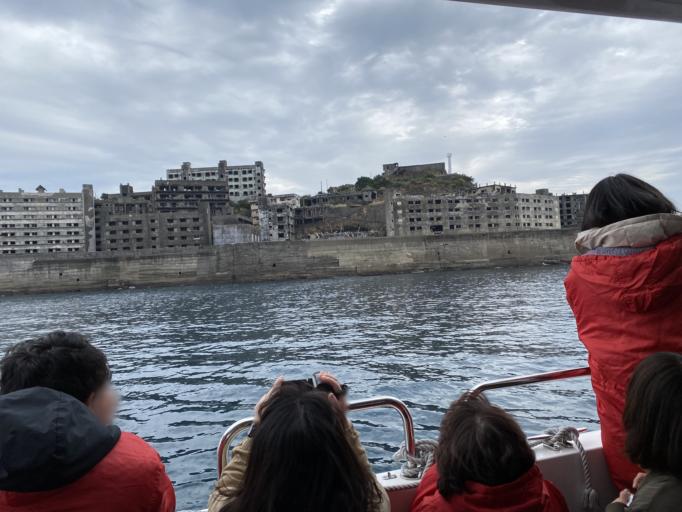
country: JP
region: Nagasaki
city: Nagasaki-shi
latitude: 32.6285
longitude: 129.7359
